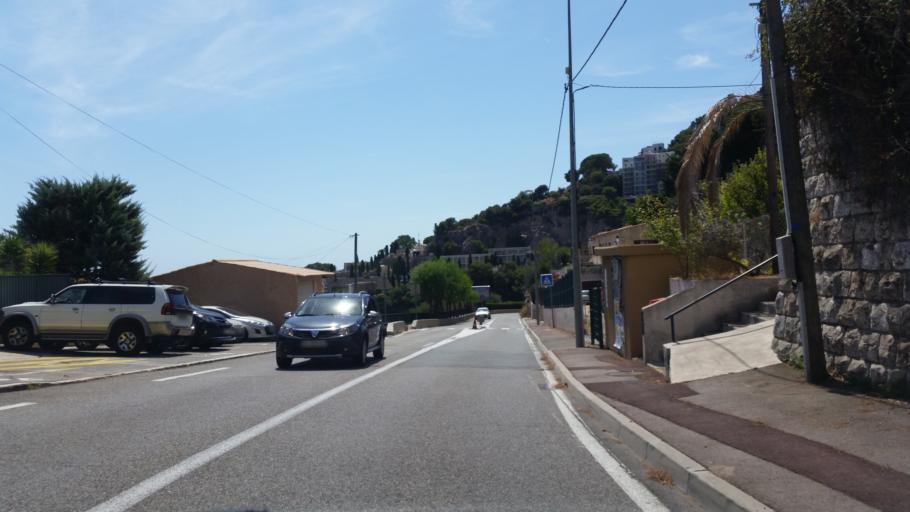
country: MC
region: Commune de Monaco
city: Saint-Roman
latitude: 43.7501
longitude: 7.4265
